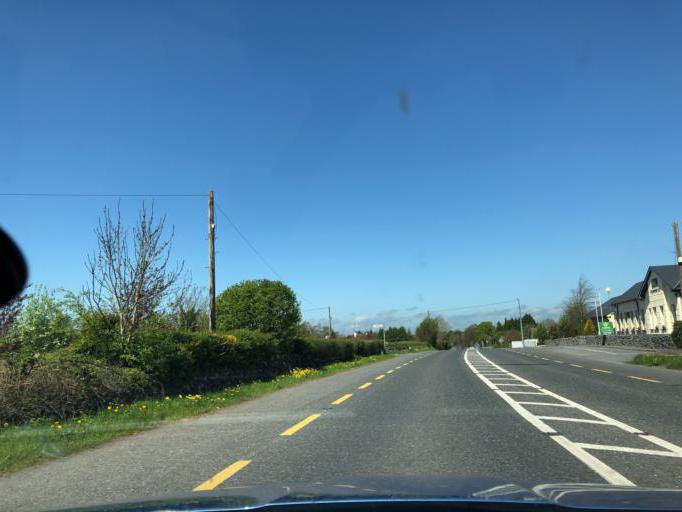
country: IE
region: Connaught
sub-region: County Galway
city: Athenry
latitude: 53.2574
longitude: -8.8062
